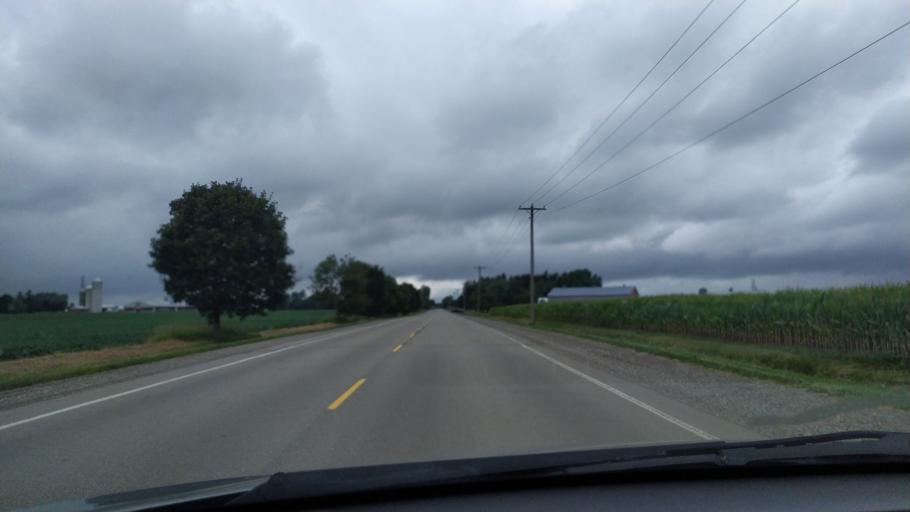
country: CA
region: Ontario
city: Kitchener
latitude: 43.3457
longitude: -80.6903
